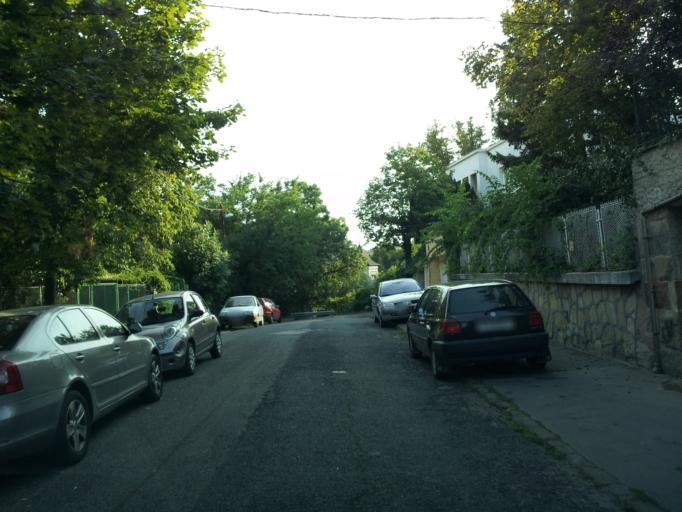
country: HU
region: Budapest
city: Budapest XII. keruelet
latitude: 47.4990
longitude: 19.0156
